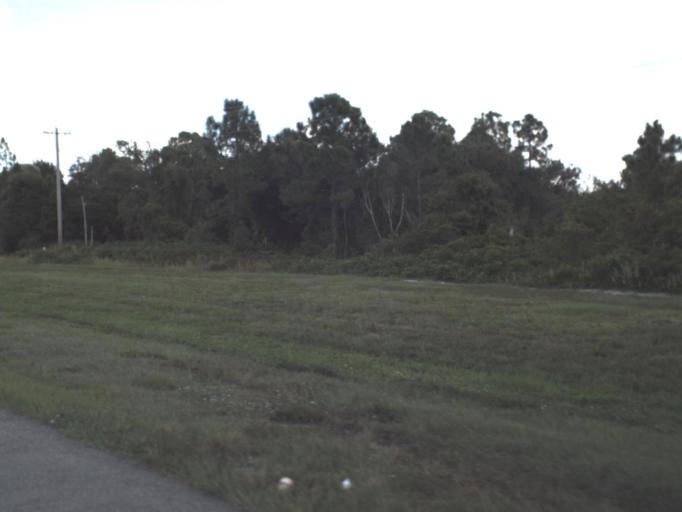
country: US
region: Florida
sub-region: Lee County
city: Lehigh Acres
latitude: 26.5472
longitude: -81.6396
